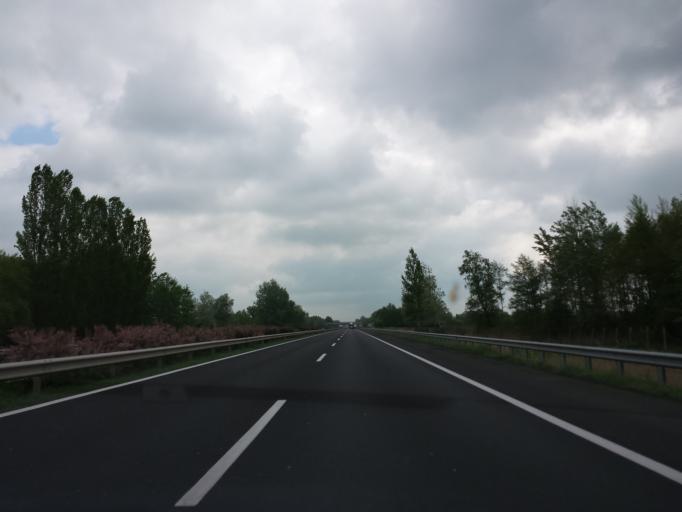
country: HU
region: Gyor-Moson-Sopron
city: Kimle
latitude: 47.7850
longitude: 17.3391
